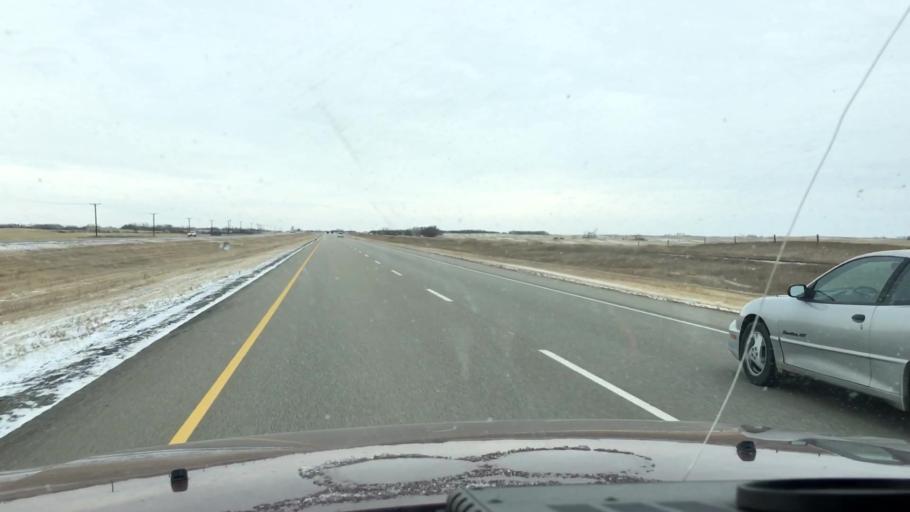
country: CA
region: Saskatchewan
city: Watrous
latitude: 51.4016
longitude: -106.1776
